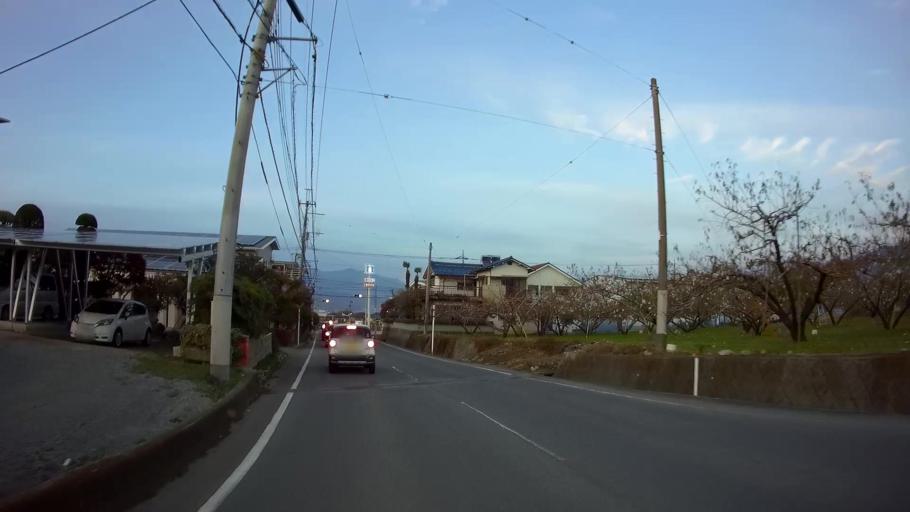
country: JP
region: Yamanashi
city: Isawa
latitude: 35.6468
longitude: 138.6874
